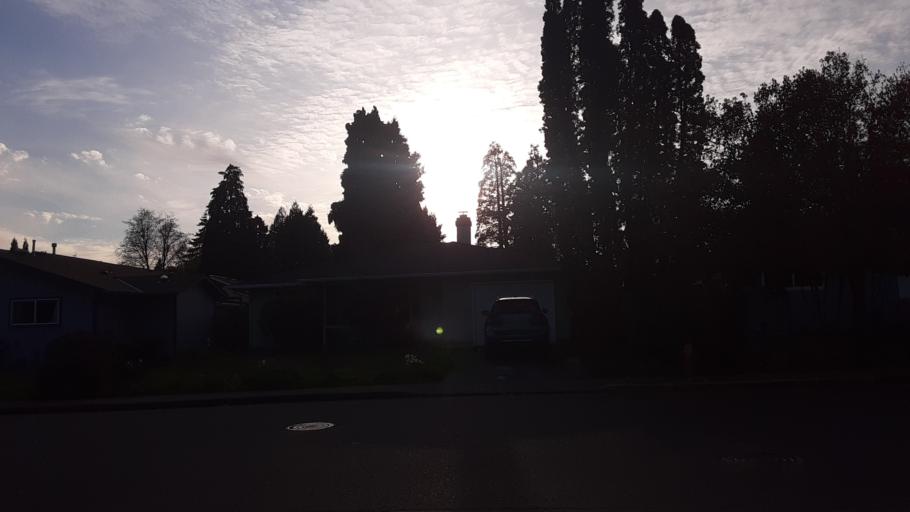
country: US
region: Oregon
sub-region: Benton County
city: Corvallis
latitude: 44.5462
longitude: -123.2592
